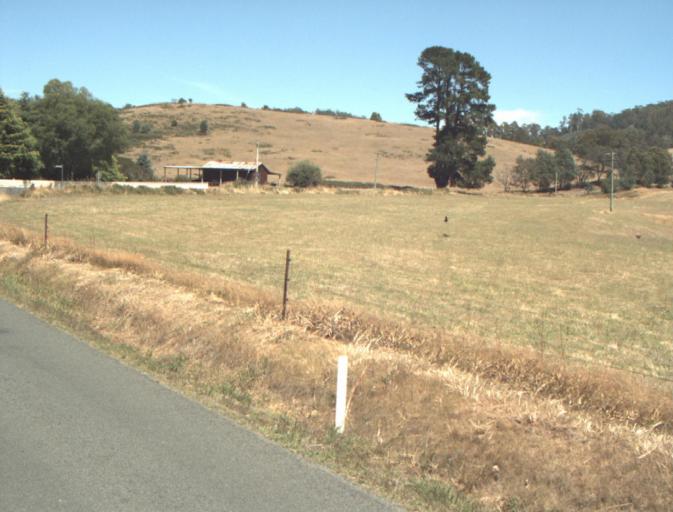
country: AU
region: Tasmania
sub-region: Launceston
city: Mayfield
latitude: -41.2648
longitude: 147.1348
